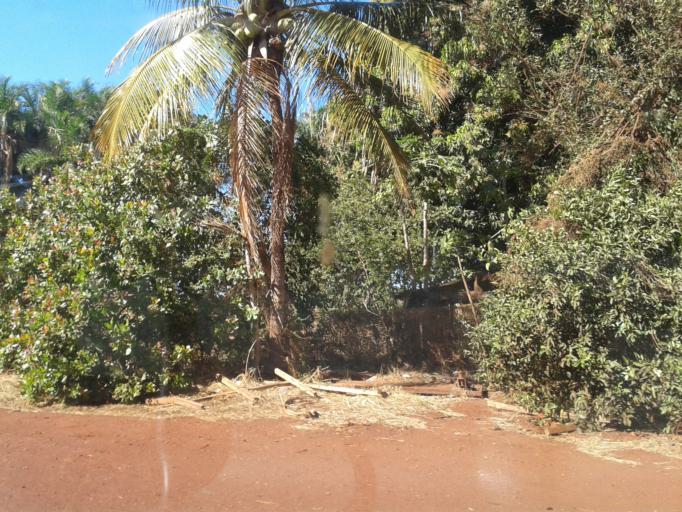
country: BR
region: Minas Gerais
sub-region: Centralina
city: Centralina
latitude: -18.5847
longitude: -49.1459
